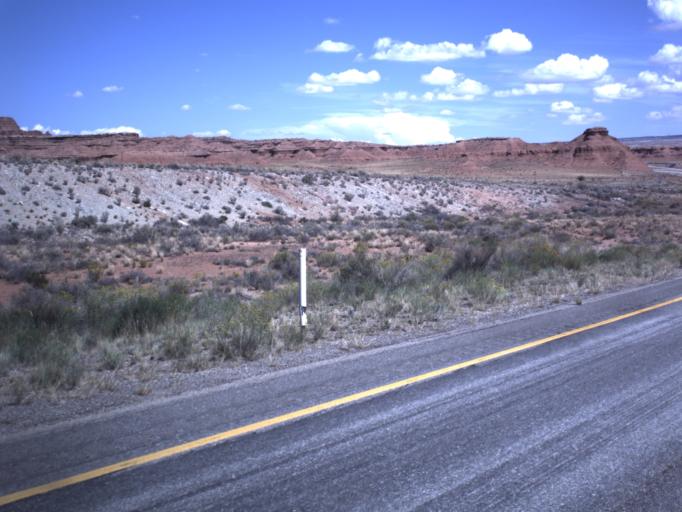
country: US
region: Utah
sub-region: Emery County
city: Ferron
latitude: 38.8385
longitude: -111.0795
